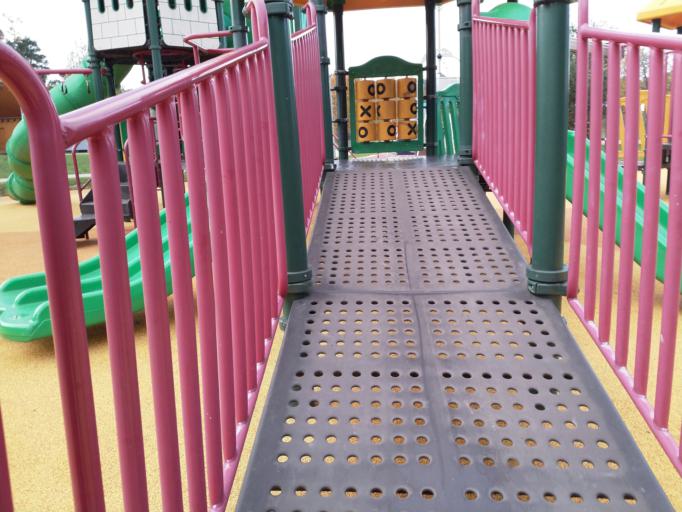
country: LV
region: Ventspils
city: Ventspils
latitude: 57.4080
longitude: 21.5932
